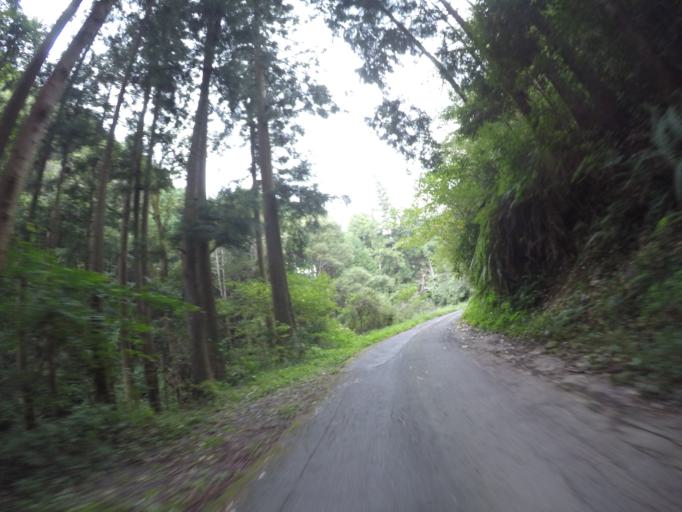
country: JP
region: Shizuoka
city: Shimada
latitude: 34.8806
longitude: 138.1734
